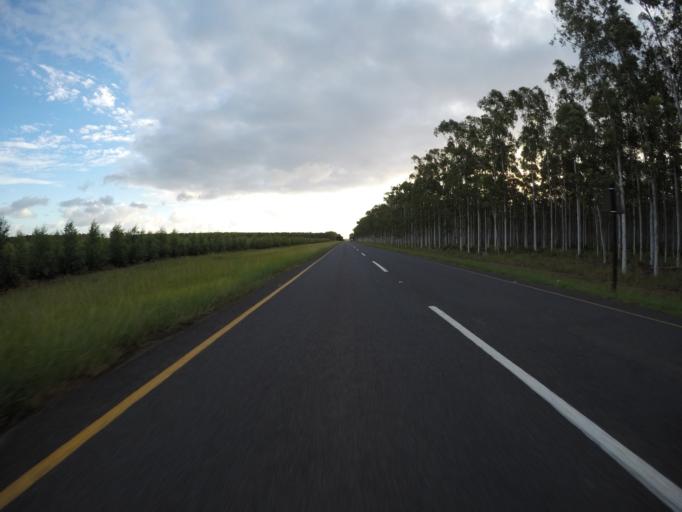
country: ZA
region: KwaZulu-Natal
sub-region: uMkhanyakude District Municipality
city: Mtubatuba
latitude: -28.4032
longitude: 32.2049
